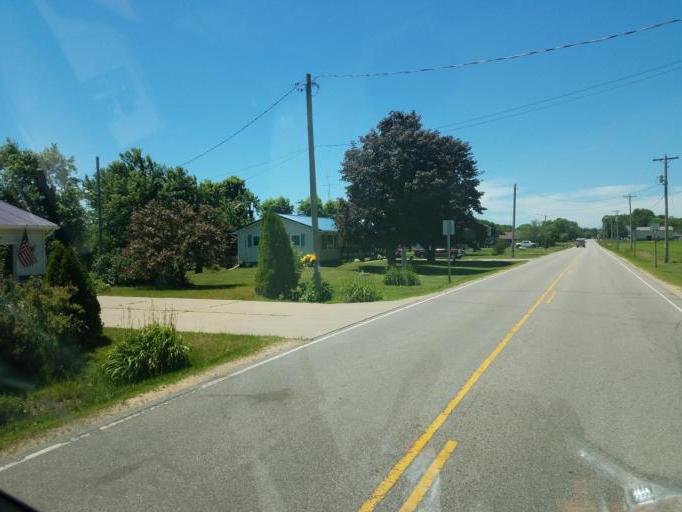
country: US
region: Wisconsin
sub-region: Juneau County
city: New Lisbon
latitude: 43.8791
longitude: -90.2631
